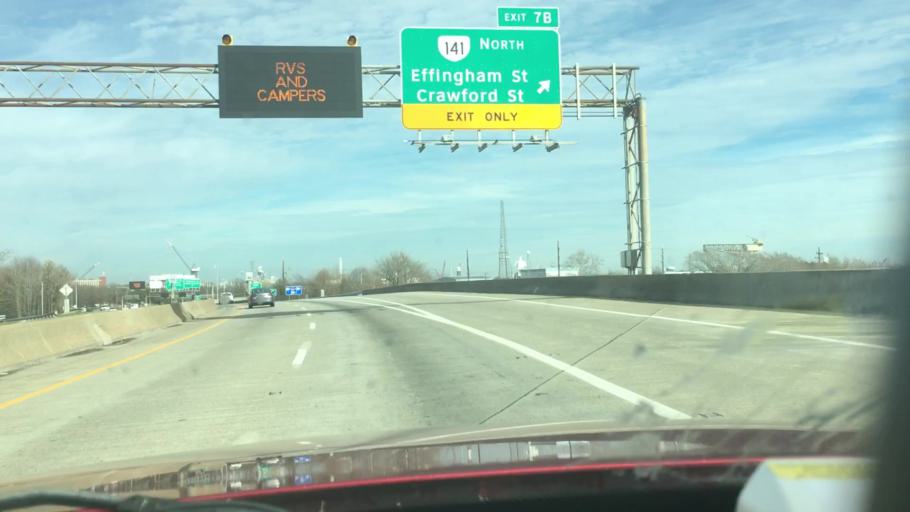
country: US
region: Virginia
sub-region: City of Portsmouth
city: Portsmouth
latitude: 36.8287
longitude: -76.3104
